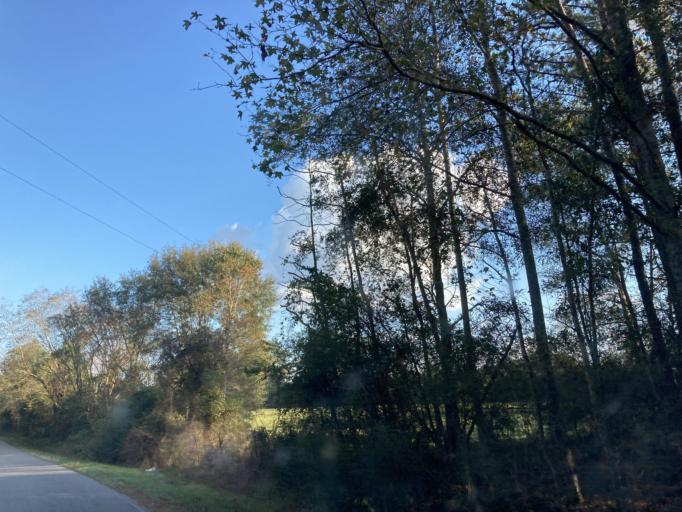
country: US
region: Mississippi
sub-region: Lamar County
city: Sumrall
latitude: 31.3897
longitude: -89.6412
